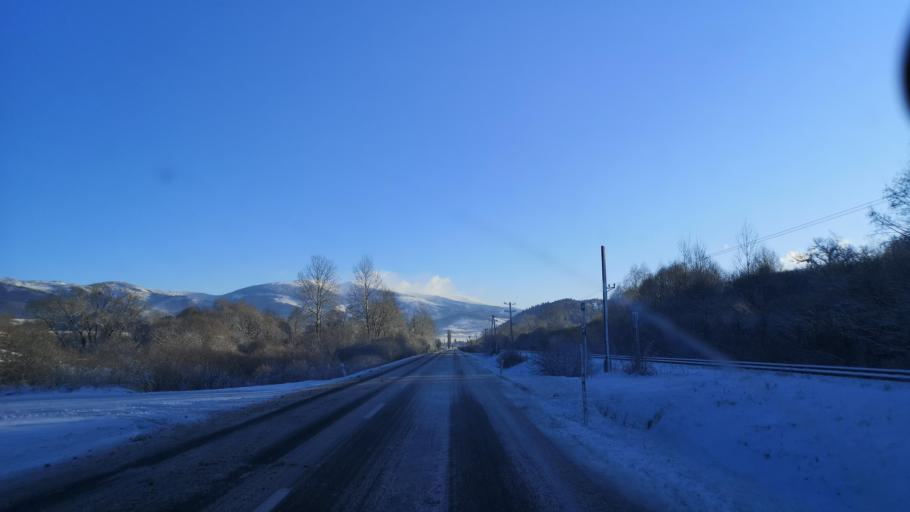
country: SK
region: Banskobystricky
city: Tisovec
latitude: 48.8532
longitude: 19.9339
